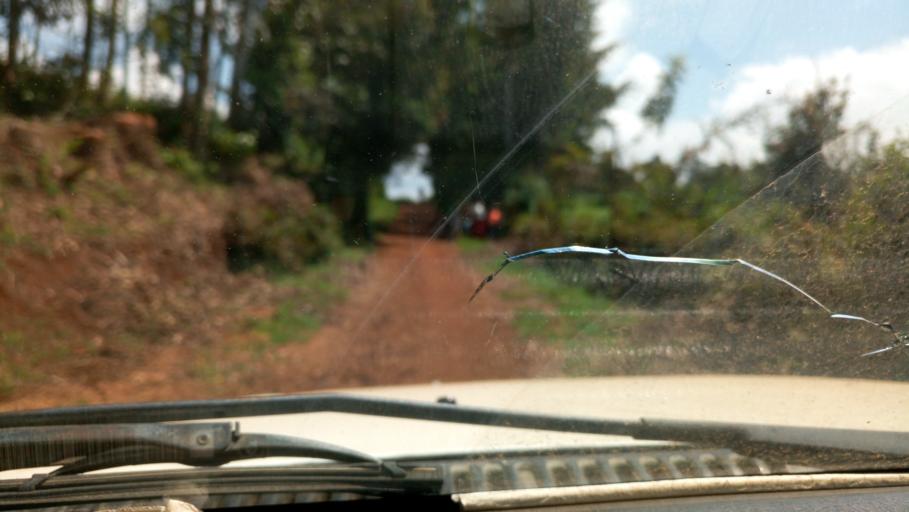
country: KE
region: Nyeri
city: Othaya
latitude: -0.6251
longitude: 36.8493
